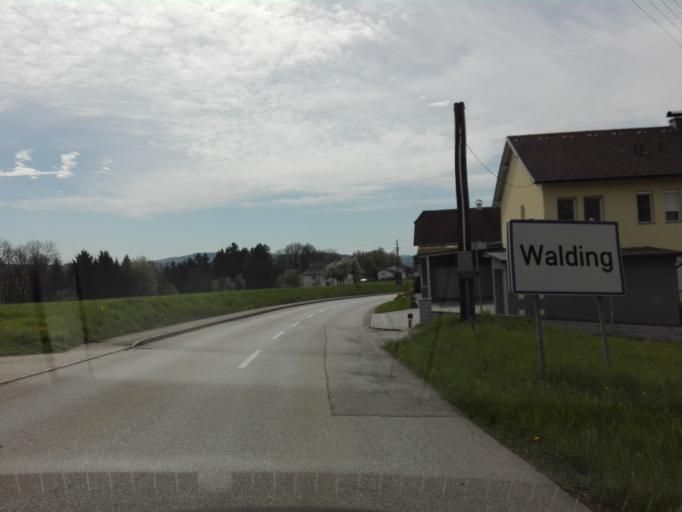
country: AT
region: Upper Austria
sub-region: Politischer Bezirk Urfahr-Umgebung
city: Walding
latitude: 48.3567
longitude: 14.1598
